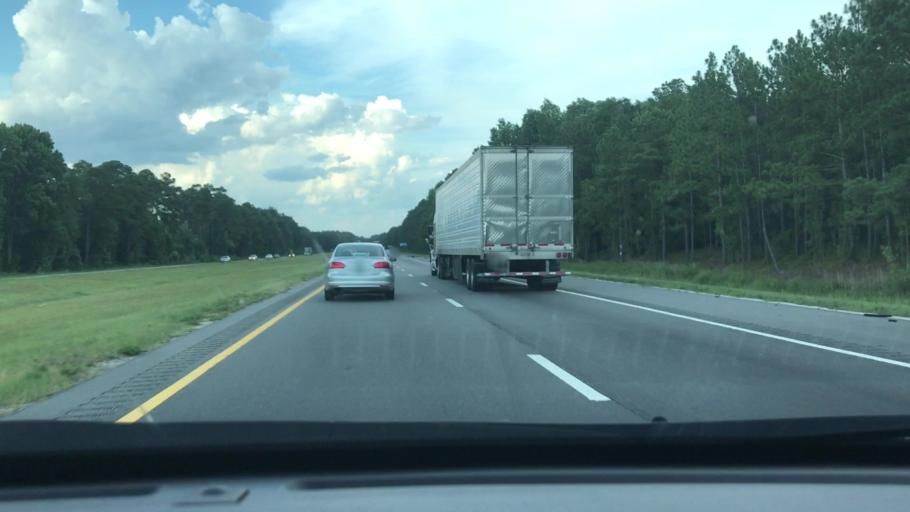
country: US
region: North Carolina
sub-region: Cumberland County
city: Hope Mills
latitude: 34.9498
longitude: -78.9033
